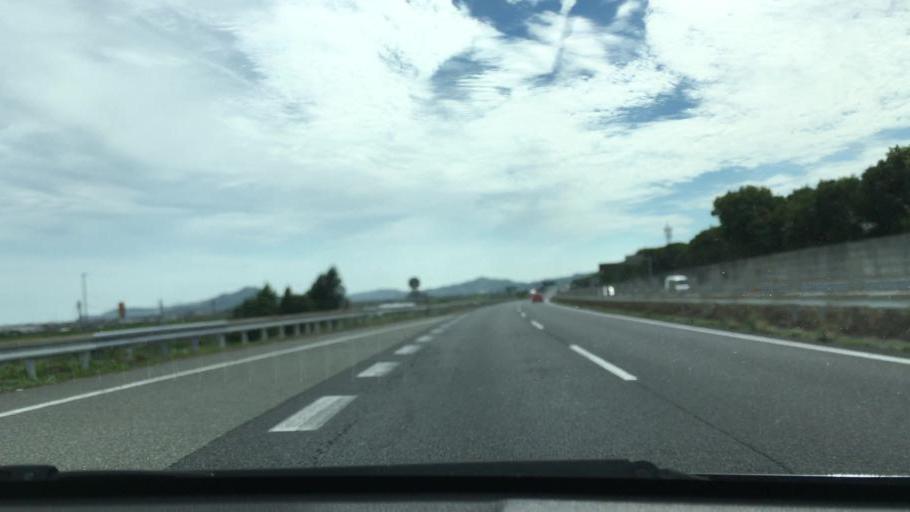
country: JP
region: Yamaguchi
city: Hofu
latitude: 34.0553
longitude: 131.5360
